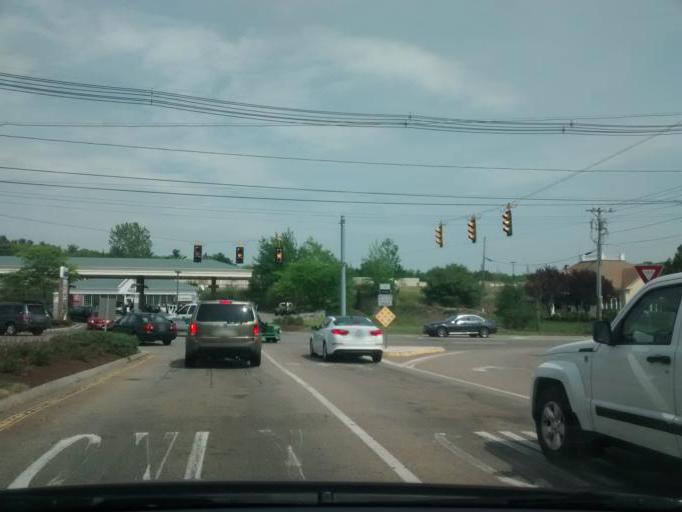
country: US
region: Massachusetts
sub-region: Norfolk County
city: Plainville
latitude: 42.0363
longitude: -71.3475
